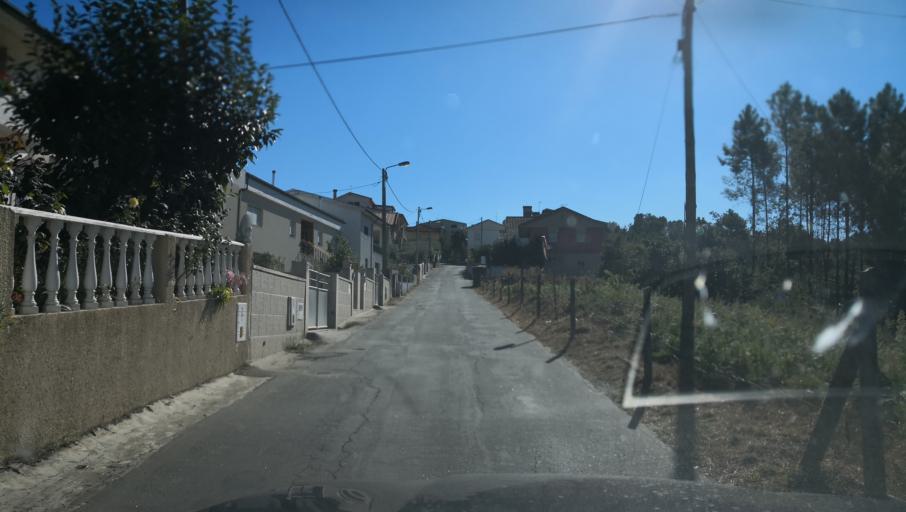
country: PT
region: Vila Real
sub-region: Vila Real
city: Vila Real
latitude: 41.2863
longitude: -7.7203
